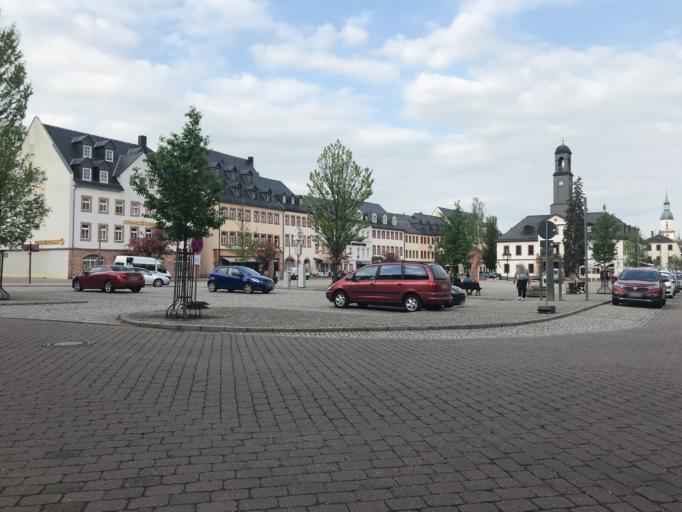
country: DE
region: Saxony
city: Rochlitz
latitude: 51.0453
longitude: 12.7981
